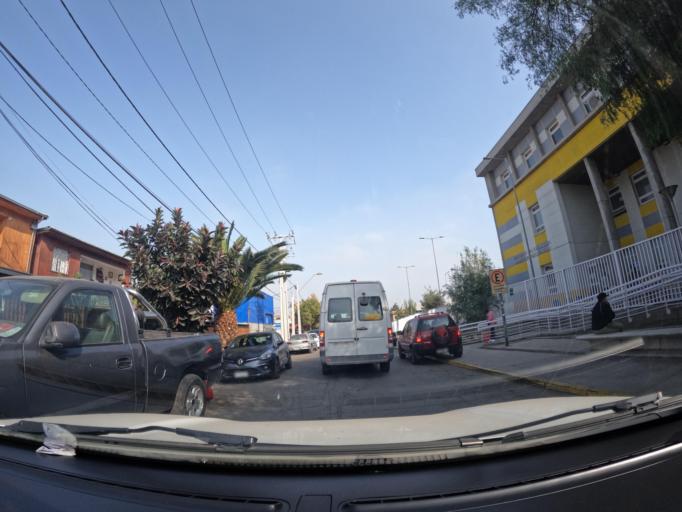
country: CL
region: Santiago Metropolitan
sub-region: Provincia de Santiago
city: Villa Presidente Frei, Nunoa, Santiago, Chile
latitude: -33.4742
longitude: -70.5742
